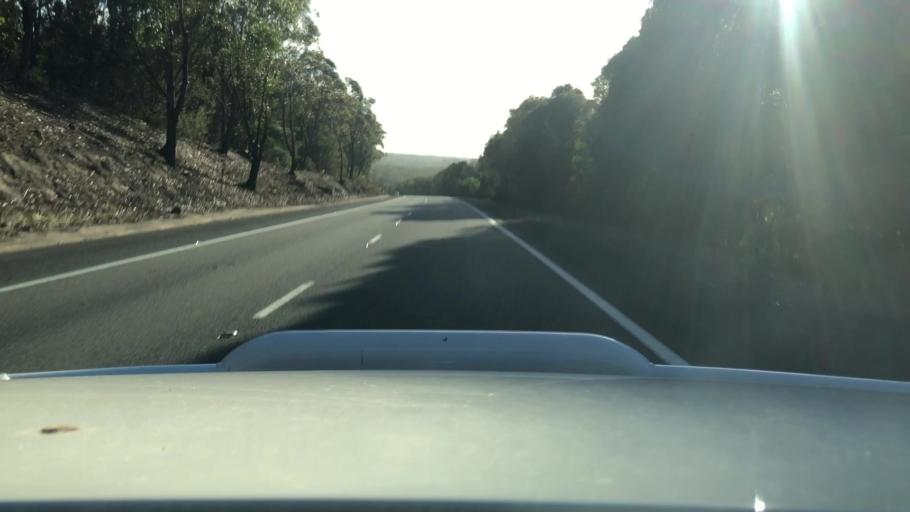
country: AU
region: New South Wales
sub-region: Wingecarribee
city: Colo Vale
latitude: -34.3944
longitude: 150.5169
